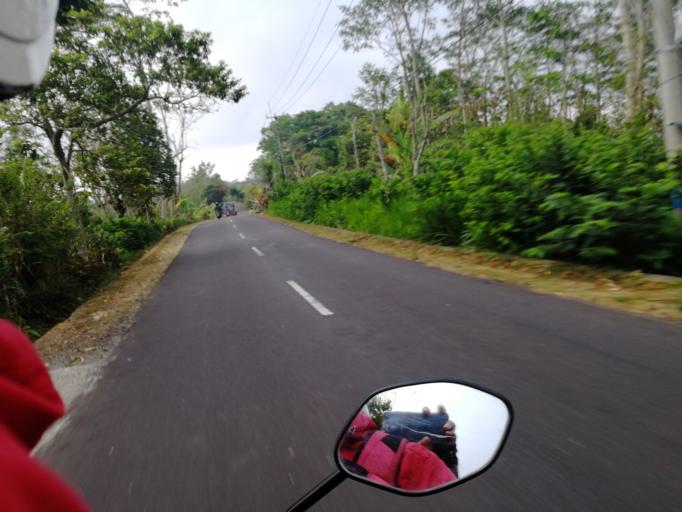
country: ID
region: Bali
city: Peneng
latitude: -8.2498
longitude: 115.2443
